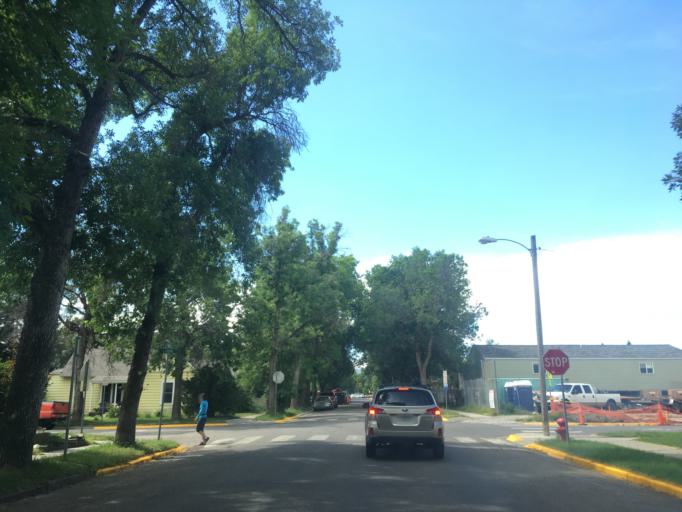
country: US
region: Montana
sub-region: Gallatin County
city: Bozeman
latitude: 45.6819
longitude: -111.0303
